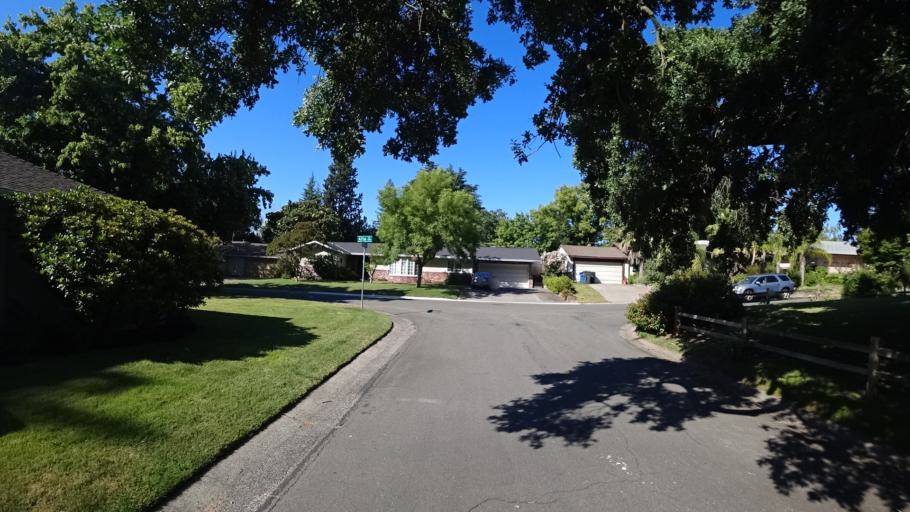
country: US
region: California
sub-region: Sacramento County
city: Sacramento
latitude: 38.5303
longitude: -121.5039
